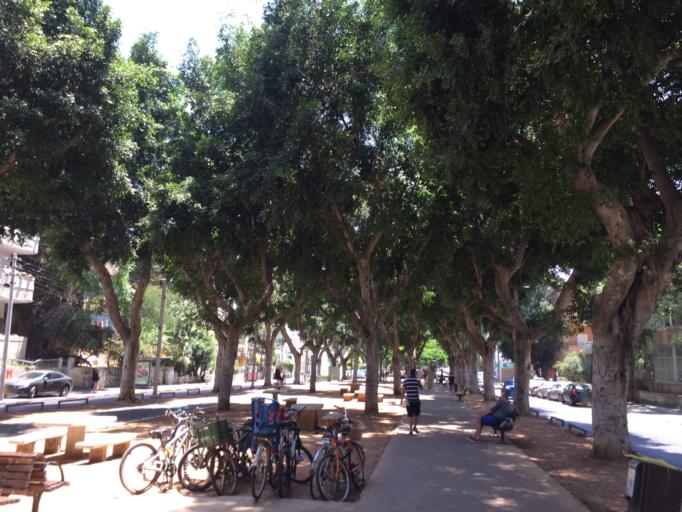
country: IL
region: Tel Aviv
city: Tel Aviv
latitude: 32.0692
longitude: 34.7783
